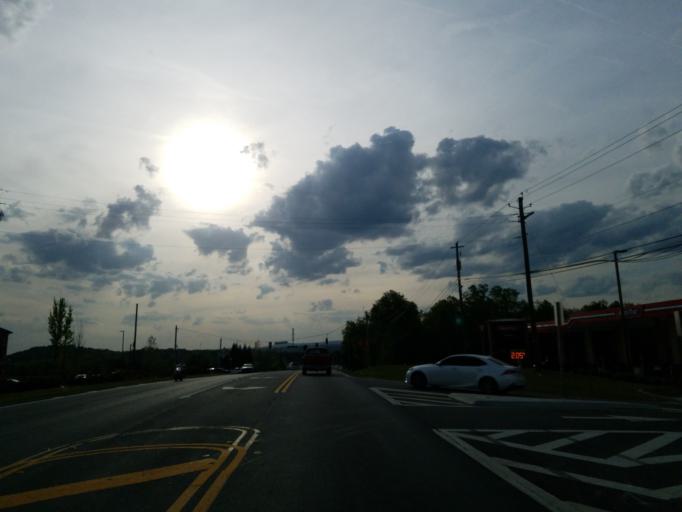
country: US
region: Georgia
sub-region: Cherokee County
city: Canton
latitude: 34.2372
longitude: -84.4562
